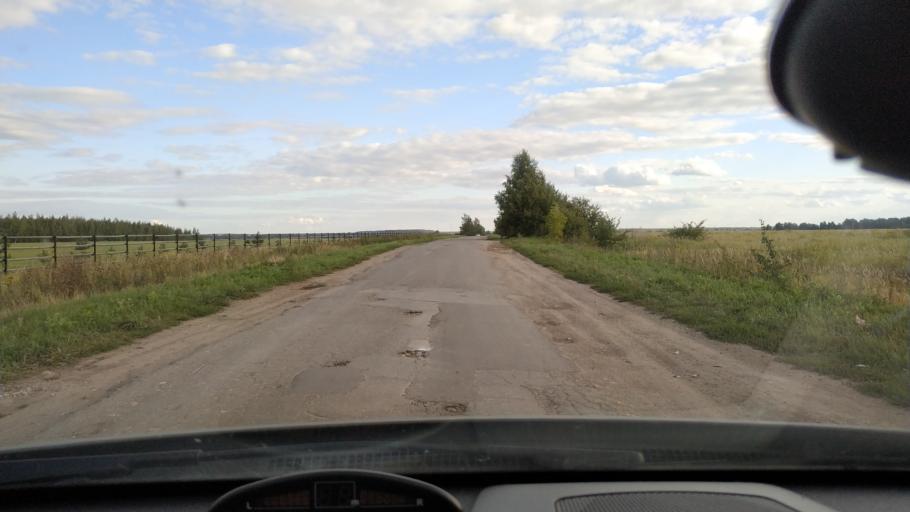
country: RU
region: Rjazan
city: Polyany
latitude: 54.5784
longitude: 39.8605
